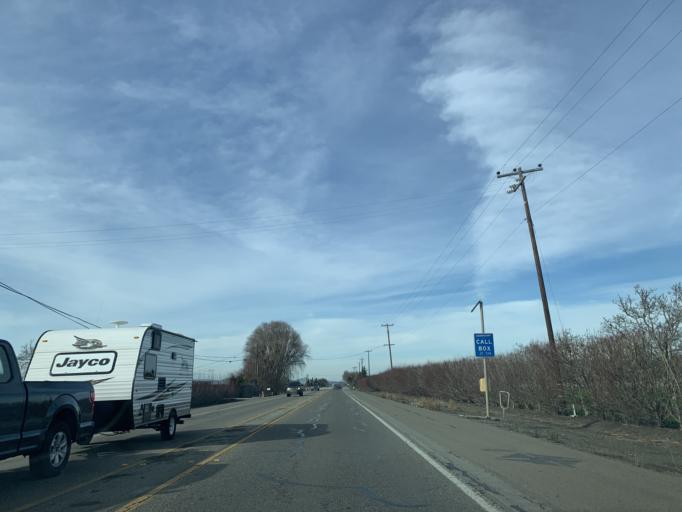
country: US
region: California
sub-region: San Benito County
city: Hollister
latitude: 36.9044
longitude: -121.4359
